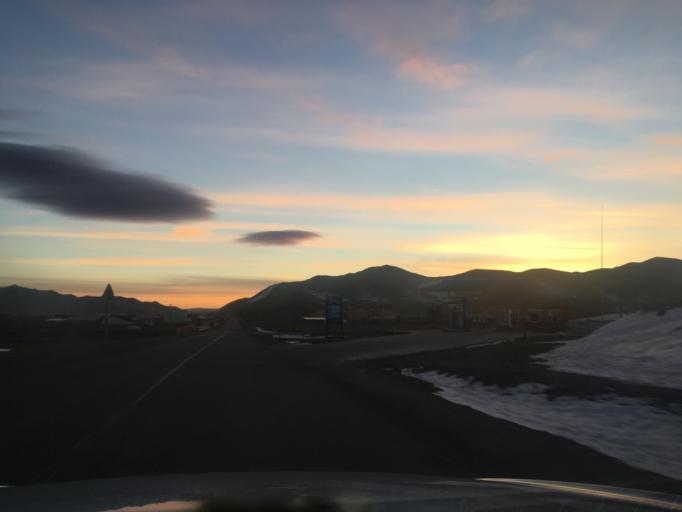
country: MN
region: Central Aimak
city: Mandal
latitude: 48.1247
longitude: 106.6545
